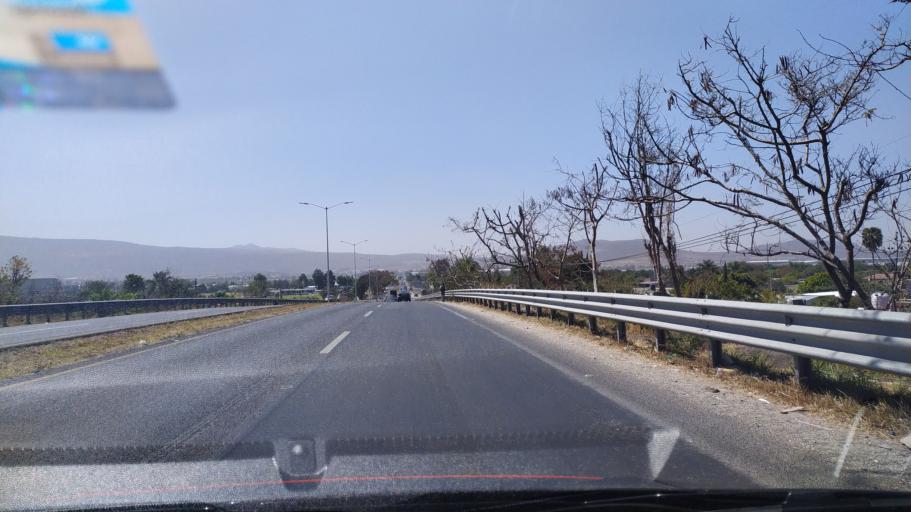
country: MX
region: Jalisco
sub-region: Tlajomulco de Zuniga
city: Santa Cruz de las Flores
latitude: 20.4796
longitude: -103.4988
